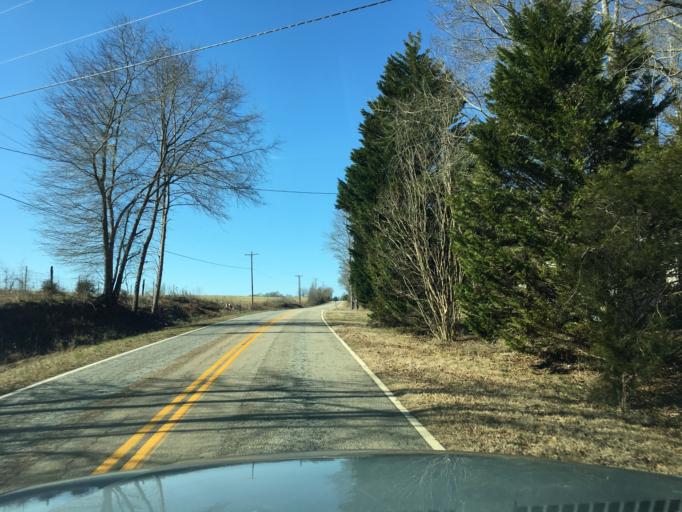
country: US
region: South Carolina
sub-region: Pickens County
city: Pickens
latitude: 34.8588
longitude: -82.7520
